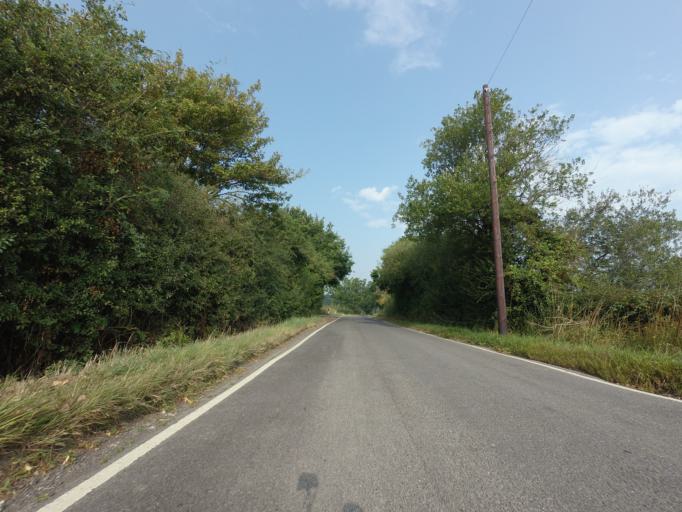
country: GB
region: England
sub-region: Kent
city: Tenterden
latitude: 51.1190
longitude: 0.6994
